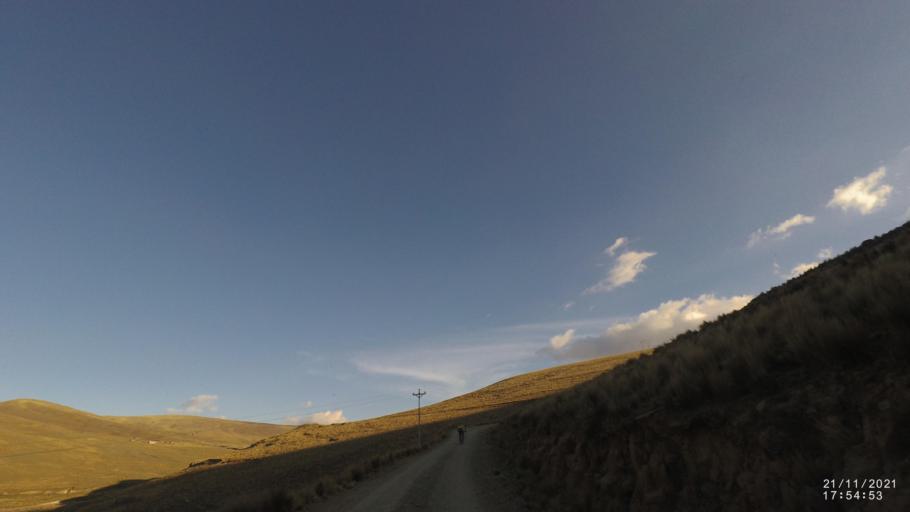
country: BO
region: Cochabamba
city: Cochabamba
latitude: -17.2209
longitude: -66.2364
